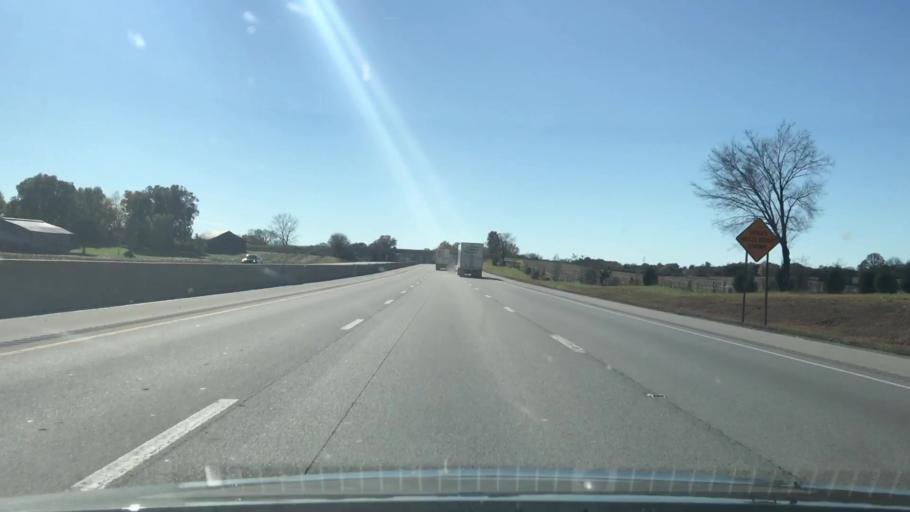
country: US
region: Kentucky
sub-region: Simpson County
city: Franklin
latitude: 36.7388
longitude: -86.5038
